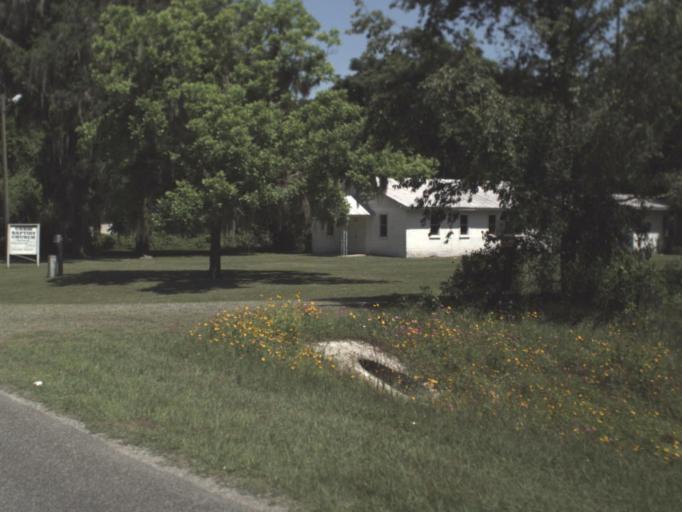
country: US
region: Florida
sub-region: Suwannee County
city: Live Oak
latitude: 30.2578
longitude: -82.9054
